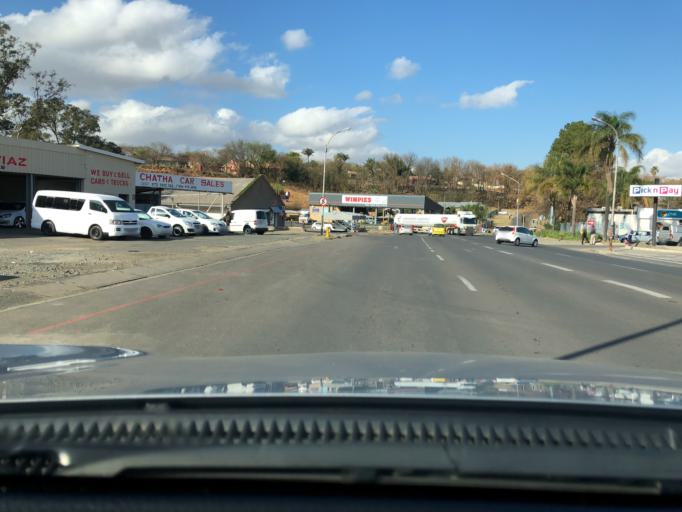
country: ZA
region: KwaZulu-Natal
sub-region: uThukela District Municipality
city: Ladysmith
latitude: -28.5563
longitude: 29.7728
